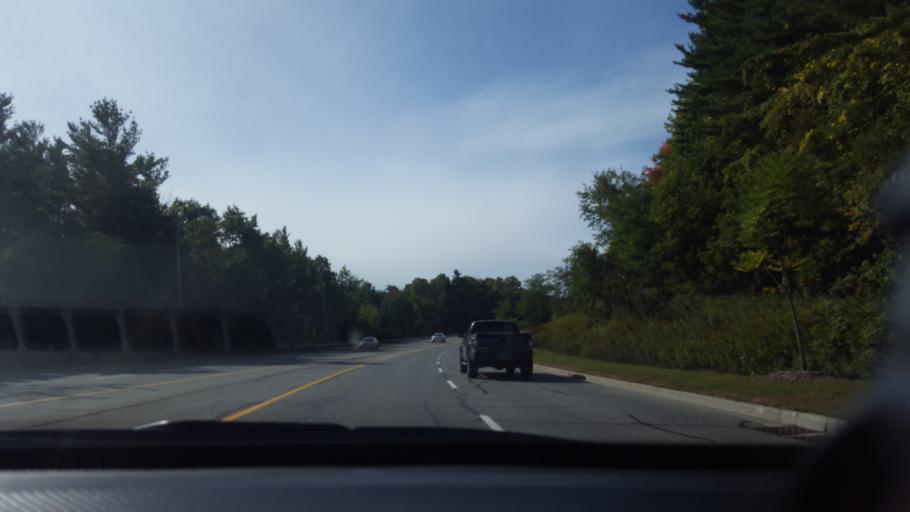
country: CA
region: Ontario
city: Newmarket
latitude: 44.0271
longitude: -79.4958
